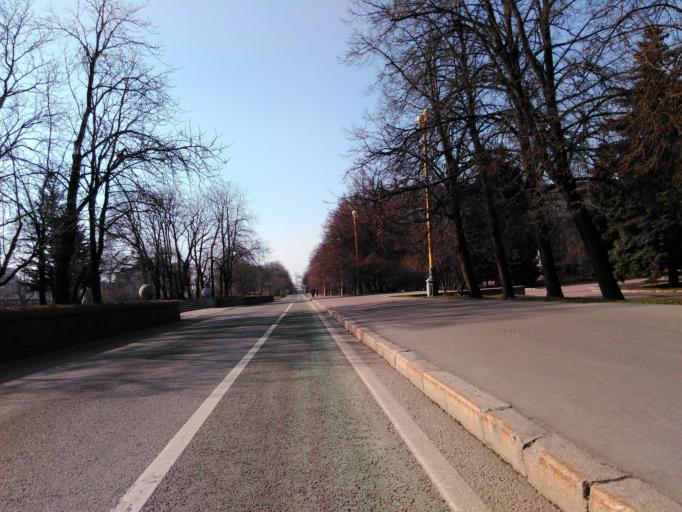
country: RU
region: Moscow
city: Vorob'yovo
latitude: 55.7000
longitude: 37.5266
